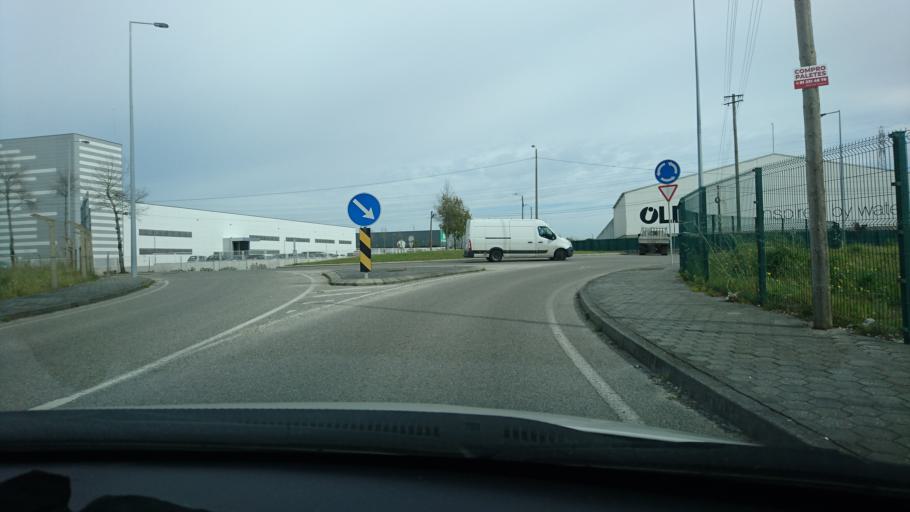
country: PT
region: Aveiro
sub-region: Aveiro
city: Eixo
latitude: 40.6457
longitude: -8.6021
